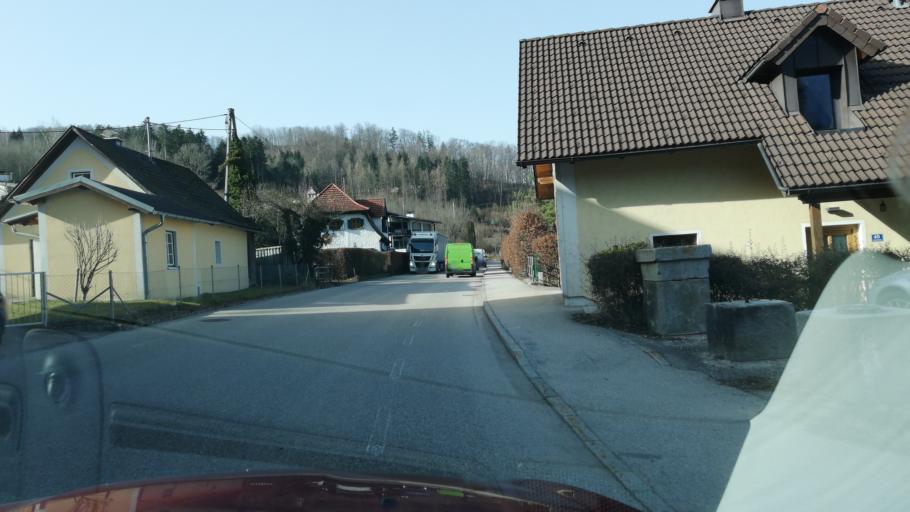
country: AT
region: Upper Austria
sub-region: Politischer Bezirk Gmunden
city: Ebensee
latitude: 47.8489
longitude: 13.7780
